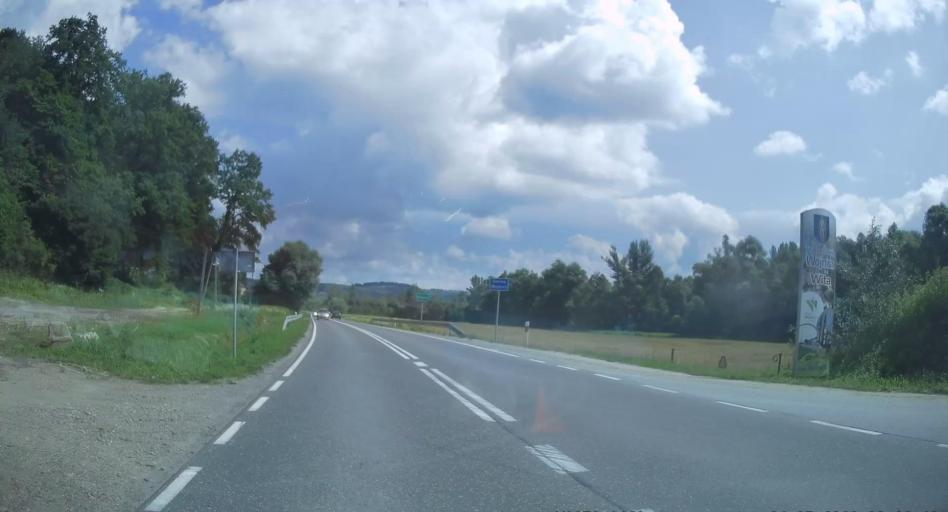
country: PL
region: Lesser Poland Voivodeship
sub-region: Powiat tarnowski
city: Zakliczyn
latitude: 49.8786
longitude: 20.8305
